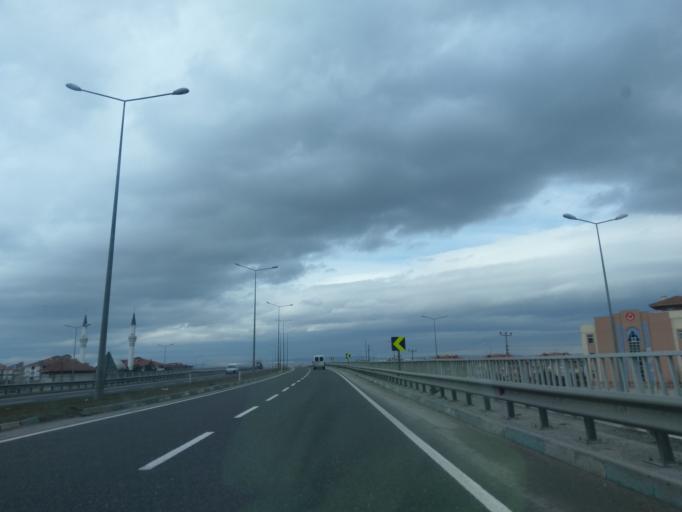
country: TR
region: Kuetahya
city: Kutahya
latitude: 39.4036
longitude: 30.0302
